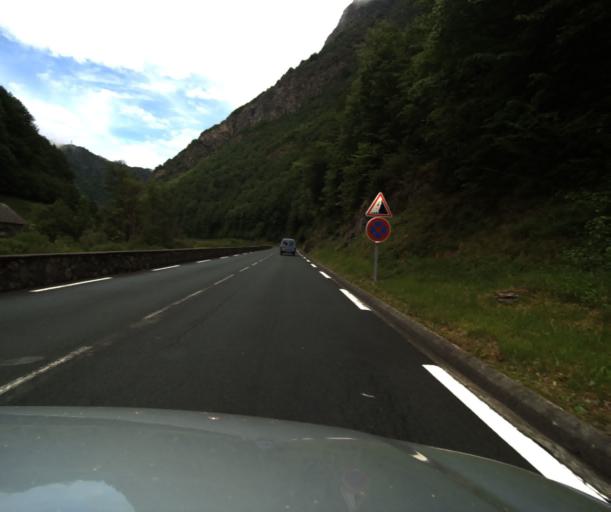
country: FR
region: Midi-Pyrenees
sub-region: Departement des Hautes-Pyrenees
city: Luz-Saint-Sauveur
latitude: 42.8024
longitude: 0.0134
